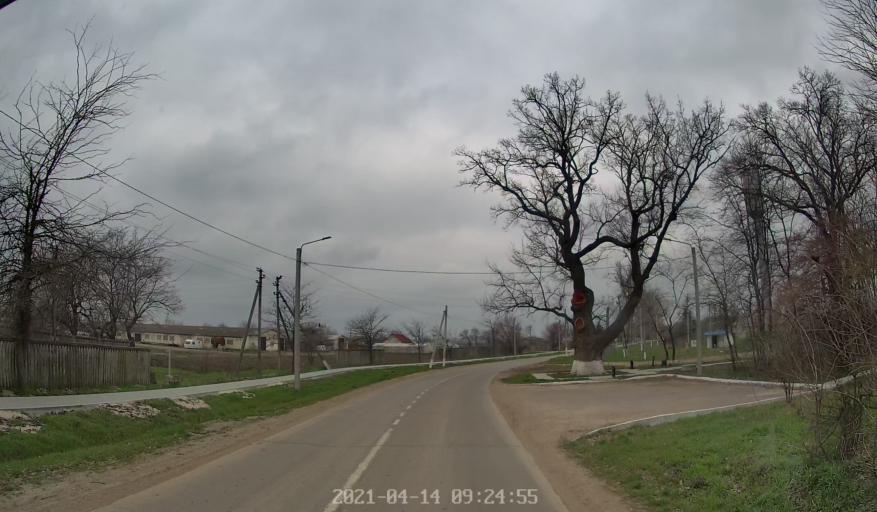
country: MD
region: Chisinau
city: Vadul lui Voda
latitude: 47.1122
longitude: 29.1124
